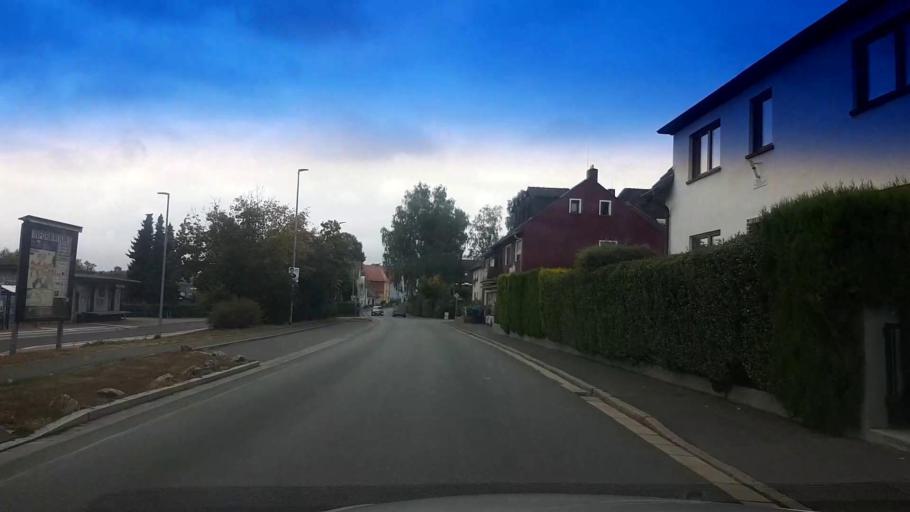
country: DE
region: Bavaria
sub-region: Upper Franconia
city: Heroldsbach
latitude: 49.6919
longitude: 11.0034
